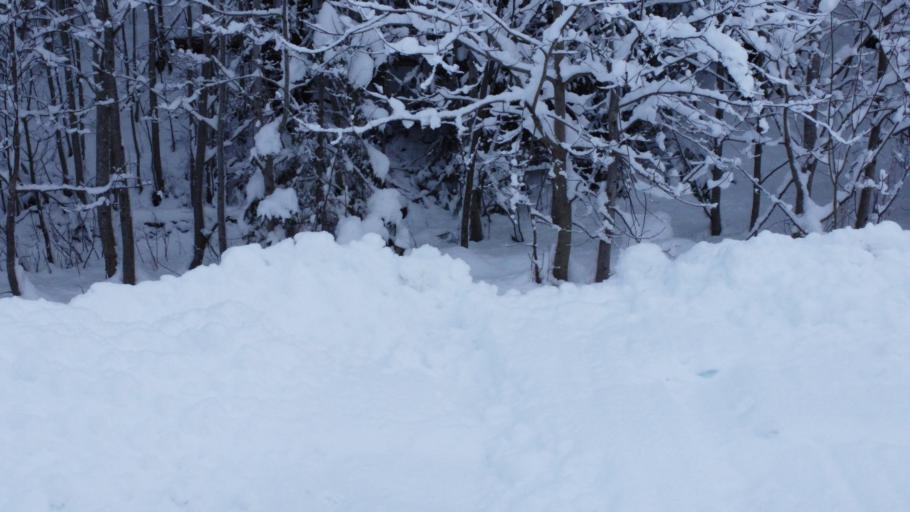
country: NO
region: Nordland
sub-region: Rana
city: Mo i Rana
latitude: 66.3355
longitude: 14.1405
